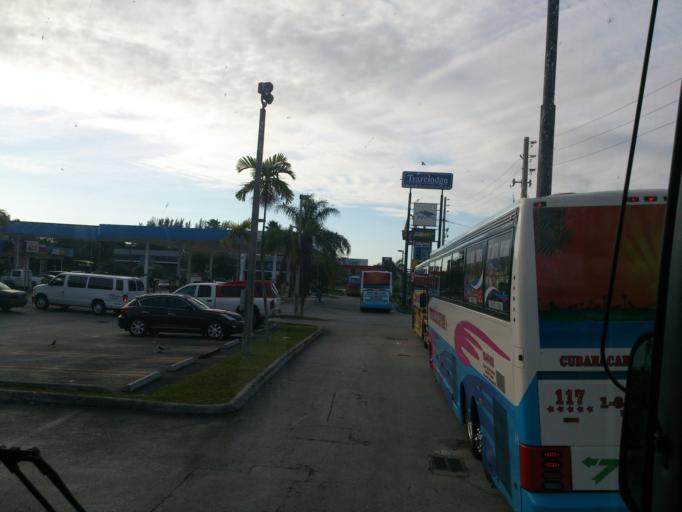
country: US
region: Florida
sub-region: Miami-Dade County
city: Florida City
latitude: 25.4437
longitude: -80.4747
